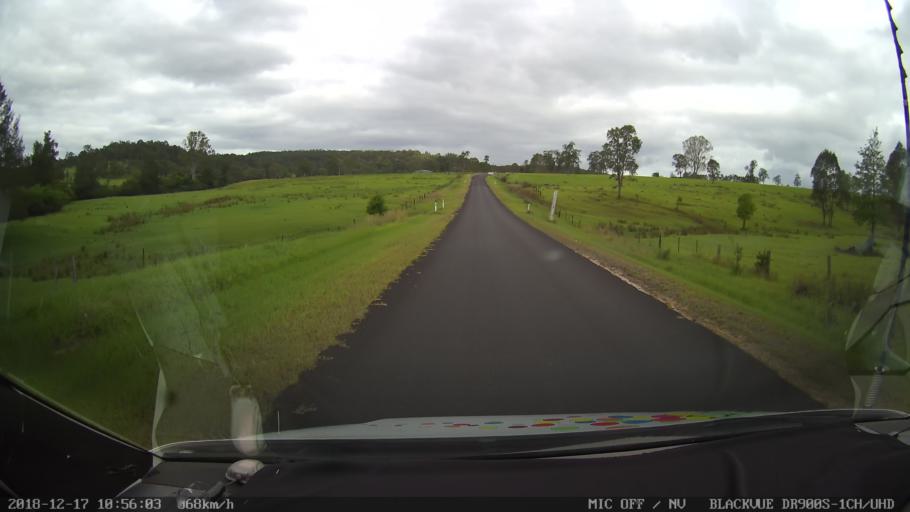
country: AU
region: New South Wales
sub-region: Richmond Valley
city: Casino
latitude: -28.8246
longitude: 152.5848
